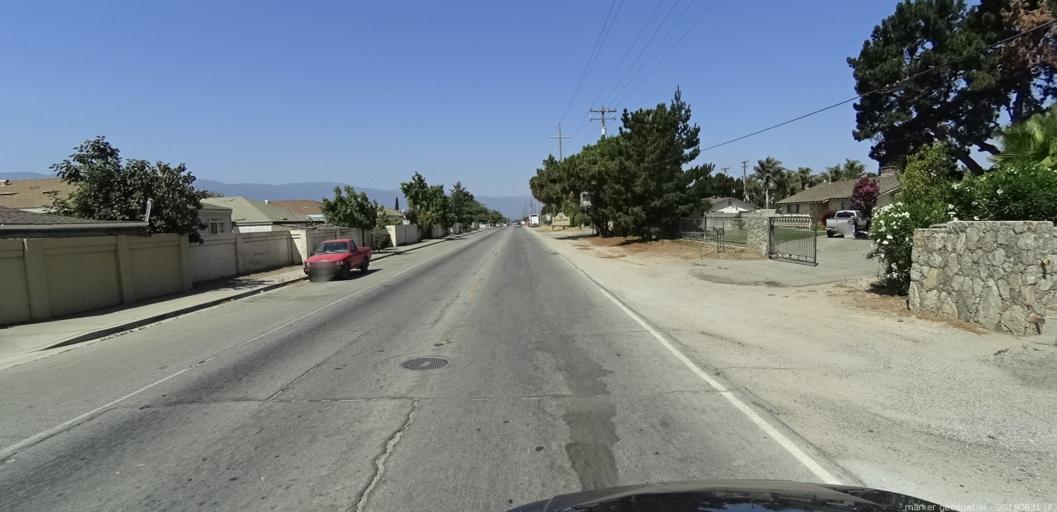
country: US
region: California
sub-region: Monterey County
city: Soledad
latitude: 36.4257
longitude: -121.3097
